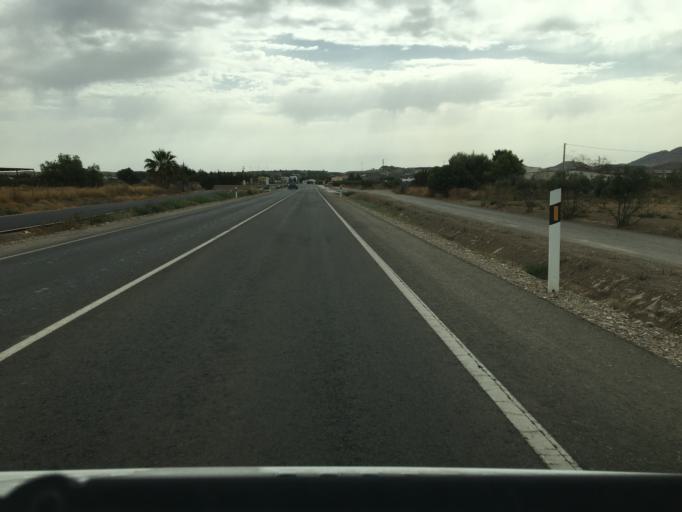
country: ES
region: Andalusia
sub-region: Provincia de Almeria
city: Huercal-Overa
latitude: 37.4146
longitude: -1.8985
